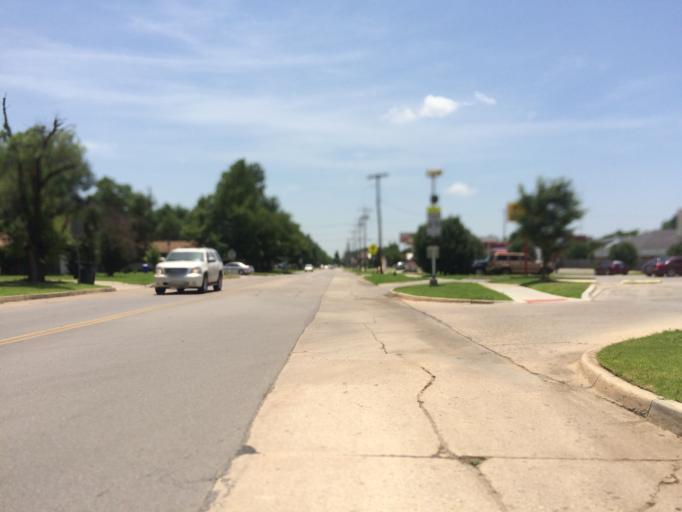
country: US
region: Oklahoma
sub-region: Cleveland County
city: Norman
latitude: 35.2286
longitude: -97.4590
